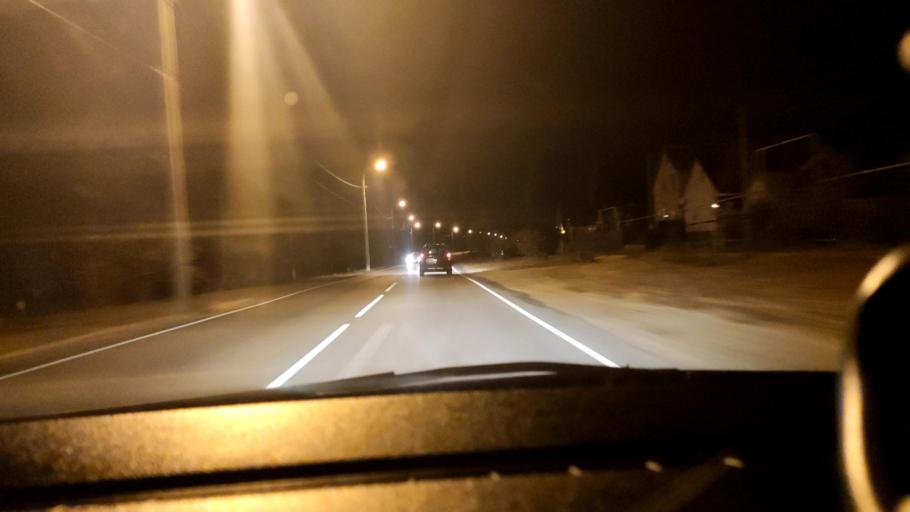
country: RU
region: Voronezj
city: Shilovo
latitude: 51.5701
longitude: 39.0447
